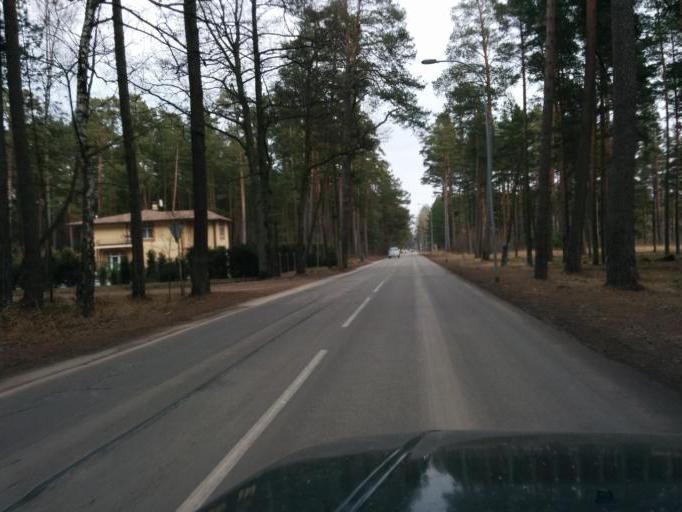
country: LV
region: Jurmala
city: Jurmala
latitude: 56.9457
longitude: 23.7299
